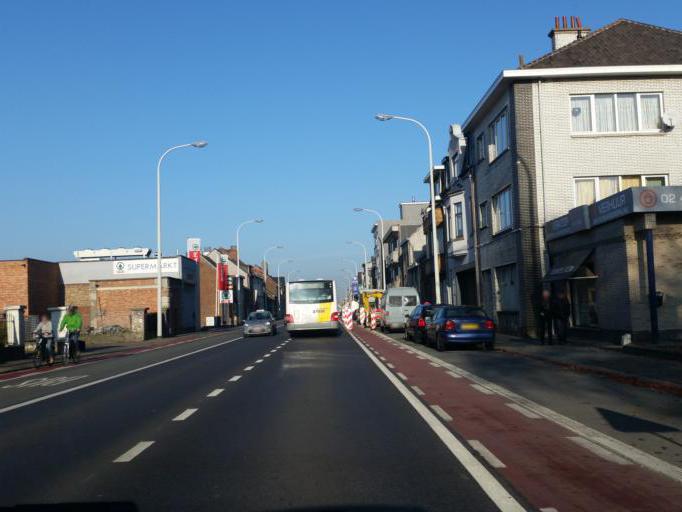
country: BE
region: Flanders
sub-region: Provincie Vlaams-Brabant
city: Asse
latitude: 50.9147
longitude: 4.1926
